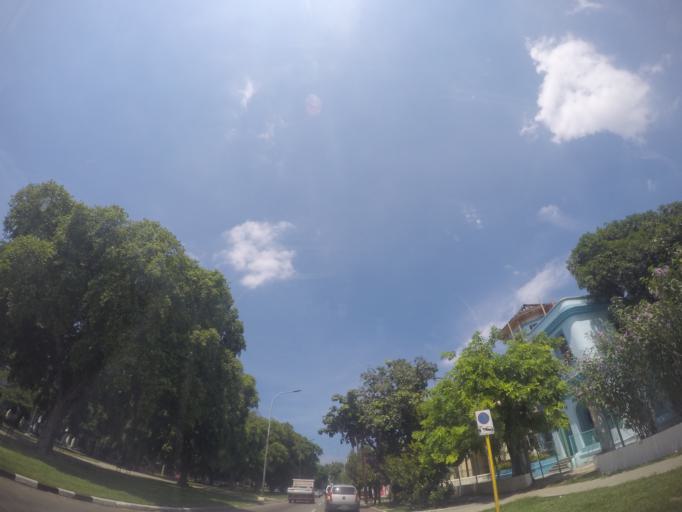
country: CU
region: La Habana
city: Havana
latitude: 23.1316
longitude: -82.3944
